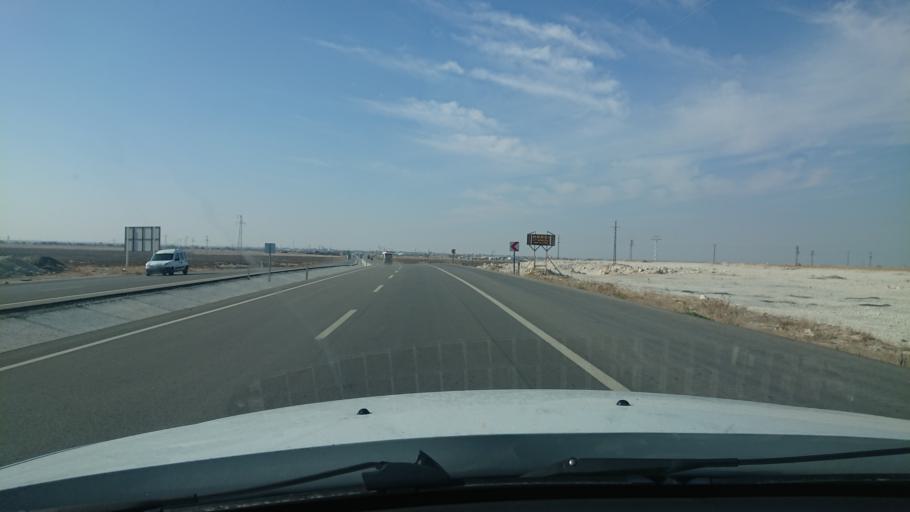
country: TR
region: Aksaray
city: Sultanhani
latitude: 38.2536
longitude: 33.4961
